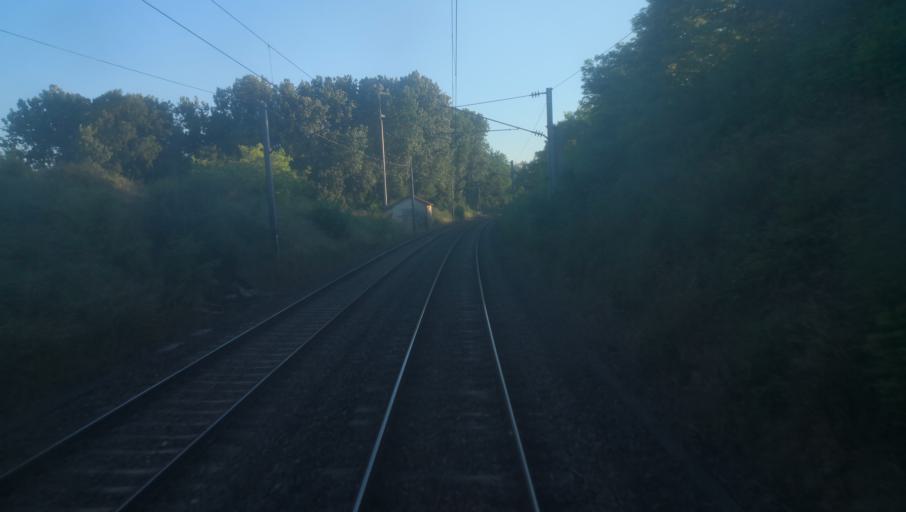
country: FR
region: Bourgogne
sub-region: Departement de la Nievre
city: Challuy
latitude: 46.9481
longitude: 3.1398
